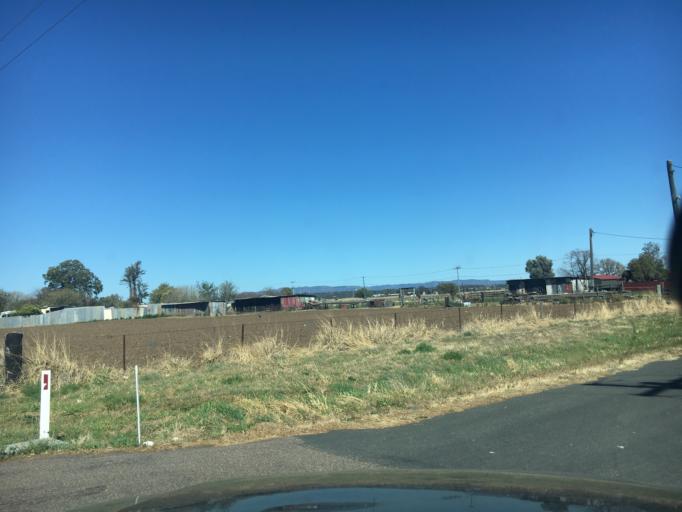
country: AU
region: New South Wales
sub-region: Singleton
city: Singleton
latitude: -32.5746
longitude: 151.1681
